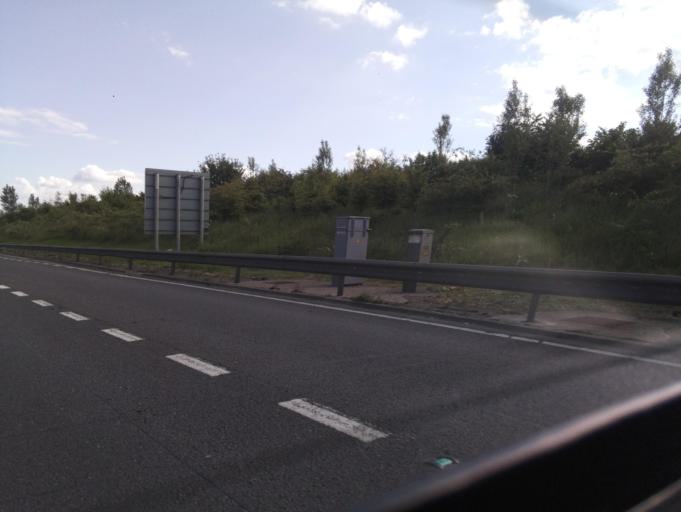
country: GB
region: England
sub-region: Central Bedfordshire
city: Toddington
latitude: 51.9642
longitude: -0.5228
